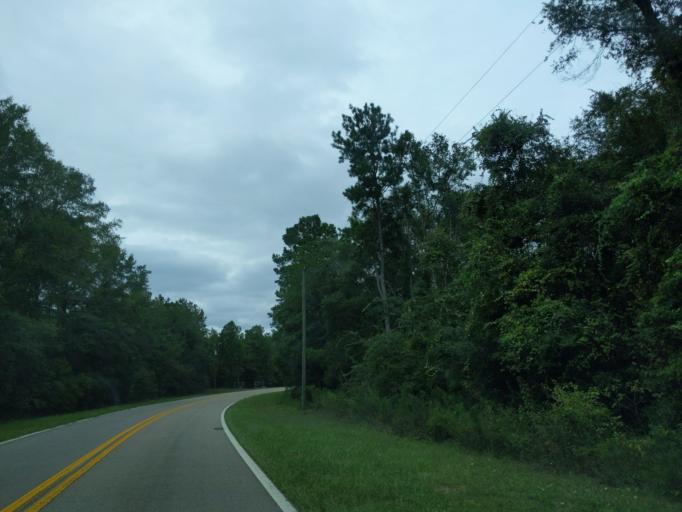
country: US
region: Florida
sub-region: Gadsden County
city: Midway
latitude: 30.4121
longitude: -84.4175
